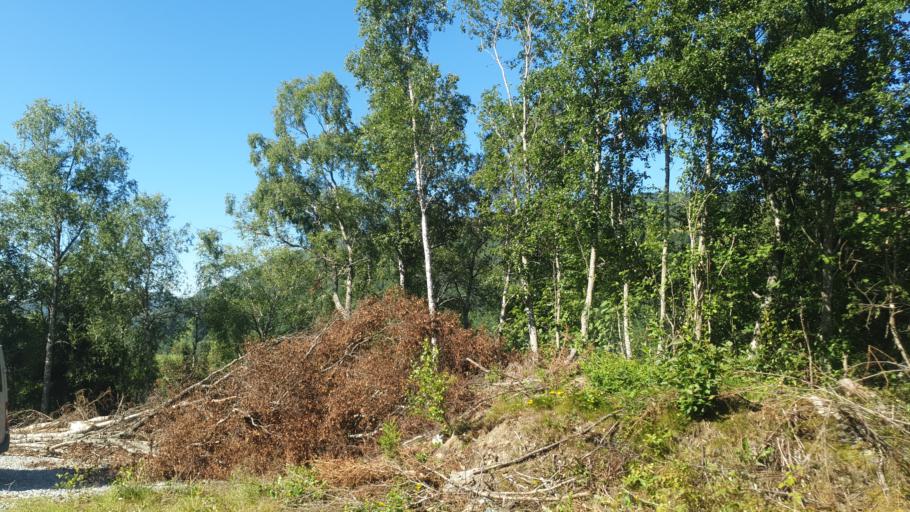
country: NO
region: Sor-Trondelag
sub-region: Meldal
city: Meldal
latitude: 63.1636
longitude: 9.7329
